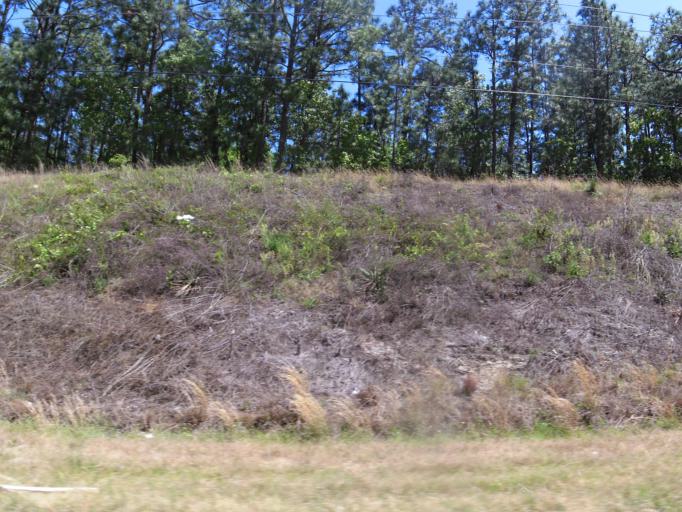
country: US
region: South Carolina
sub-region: Aiken County
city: Gloverville
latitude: 33.5345
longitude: -81.8374
